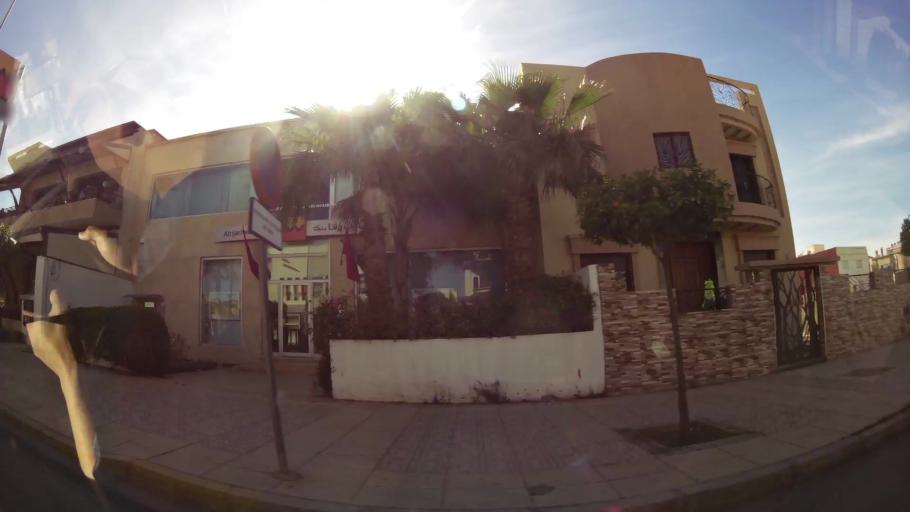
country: MA
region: Oriental
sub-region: Oujda-Angad
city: Oujda
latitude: 34.6645
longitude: -1.9067
